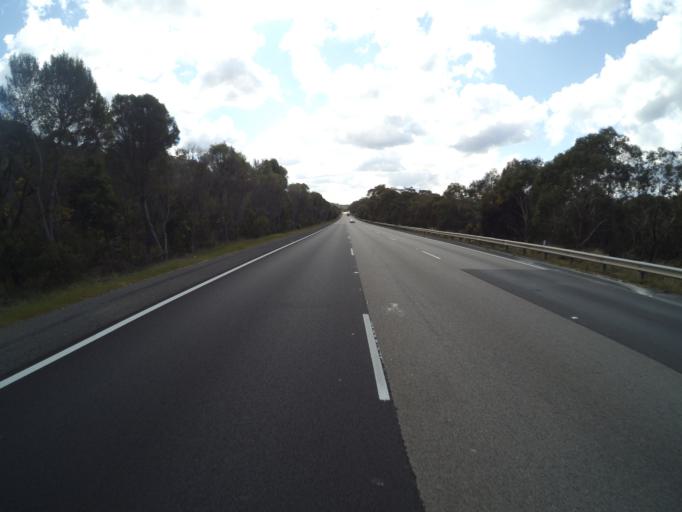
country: AU
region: New South Wales
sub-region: Wingecarribee
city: Colo Vale
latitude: -34.3887
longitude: 150.5212
